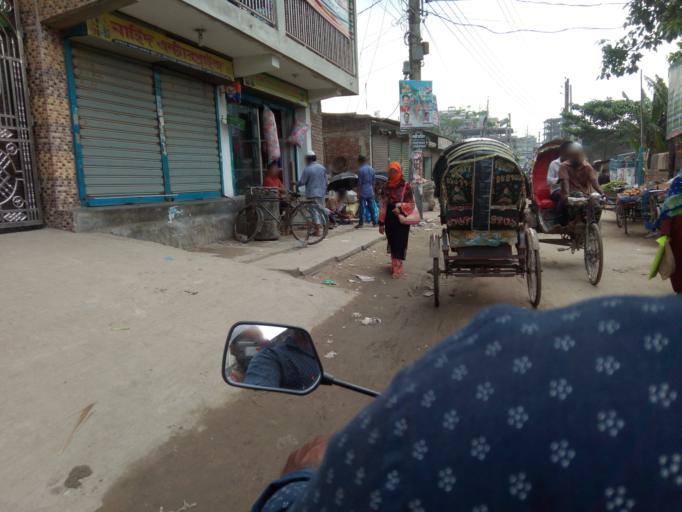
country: BD
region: Dhaka
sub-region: Dhaka
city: Dhaka
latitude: 23.7026
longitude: 90.4529
